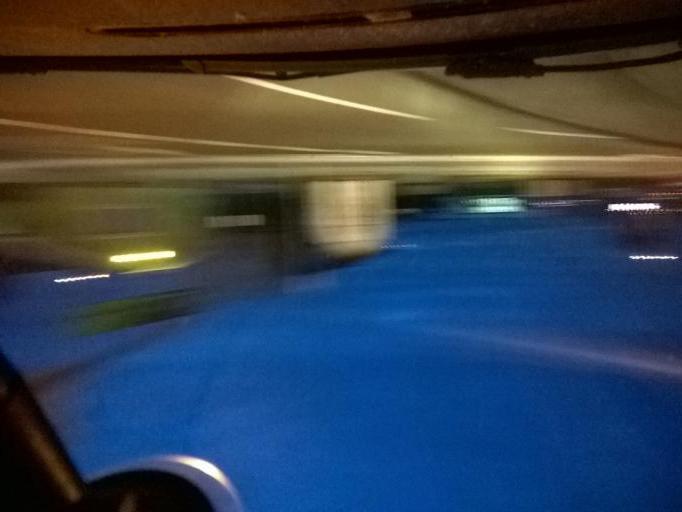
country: SI
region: Ptuj
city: Ptuj
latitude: 46.4166
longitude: 15.8856
